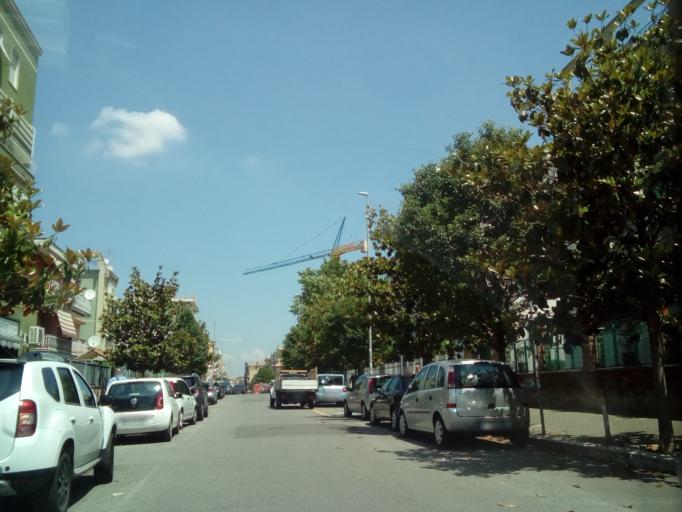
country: IT
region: Latium
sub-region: Citta metropolitana di Roma Capitale
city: Rome
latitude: 41.8802
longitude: 12.5692
